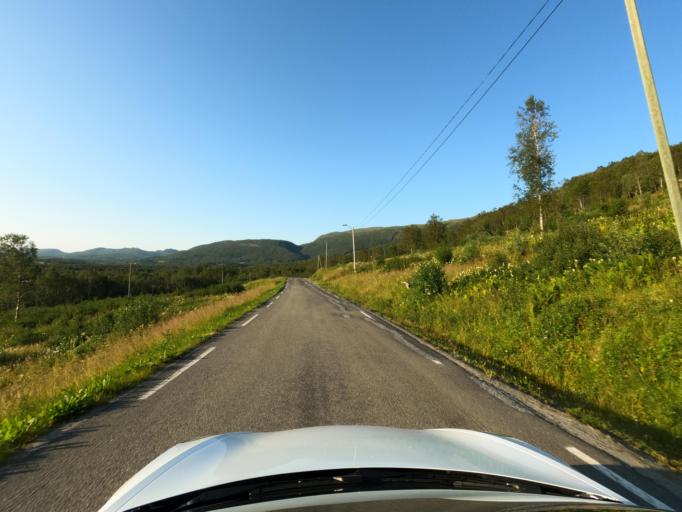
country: NO
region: Nordland
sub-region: Ballangen
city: Ballangen
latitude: 68.5204
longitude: 16.7593
